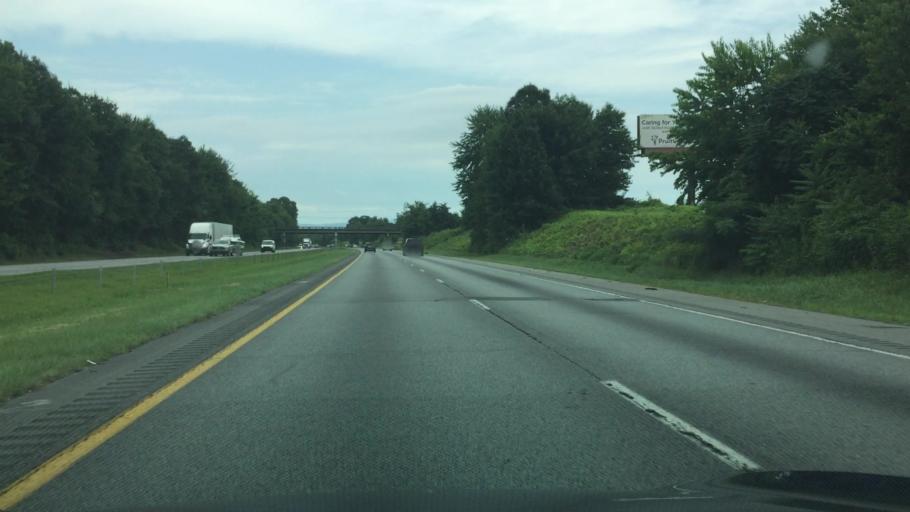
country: US
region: North Carolina
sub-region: Yadkin County
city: Jonesville
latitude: 36.2125
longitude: -80.8107
